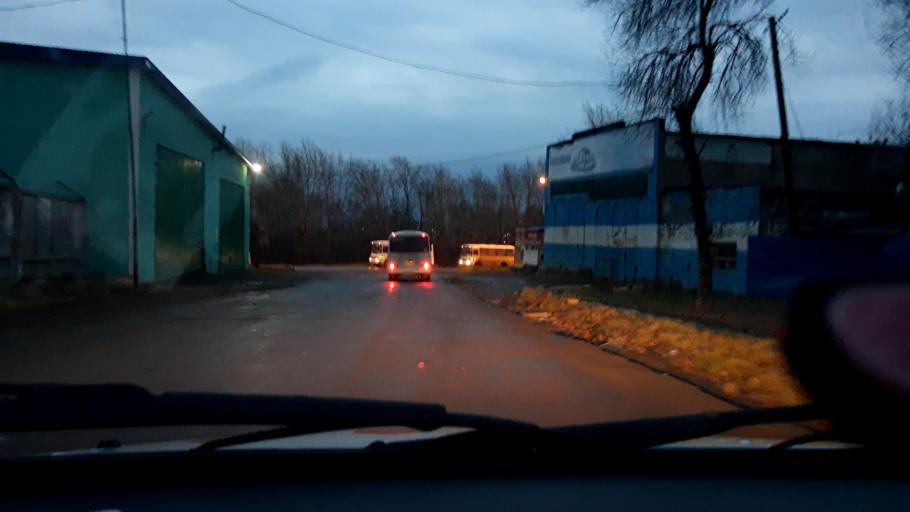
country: RU
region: Bashkortostan
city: Blagoveshchensk
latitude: 54.8900
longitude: 56.0923
